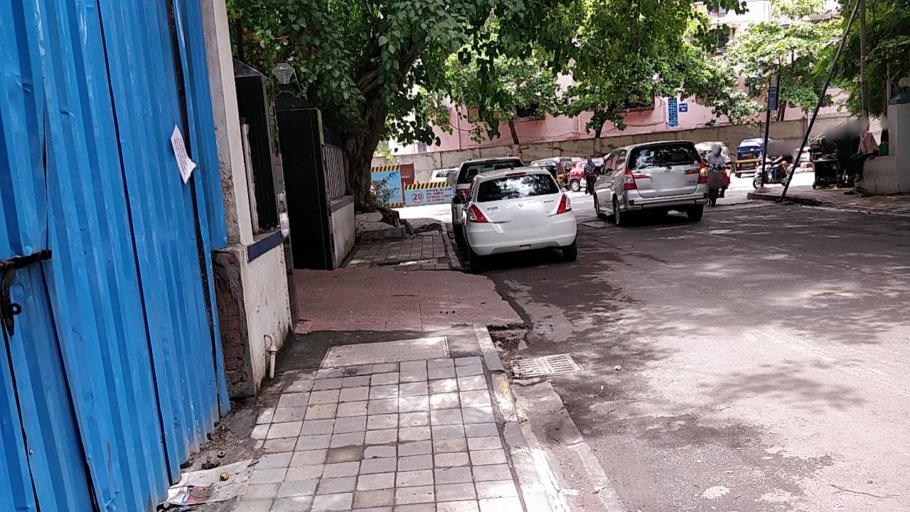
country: IN
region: Maharashtra
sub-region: Mumbai Suburban
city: Mumbai
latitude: 19.0639
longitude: 72.8370
